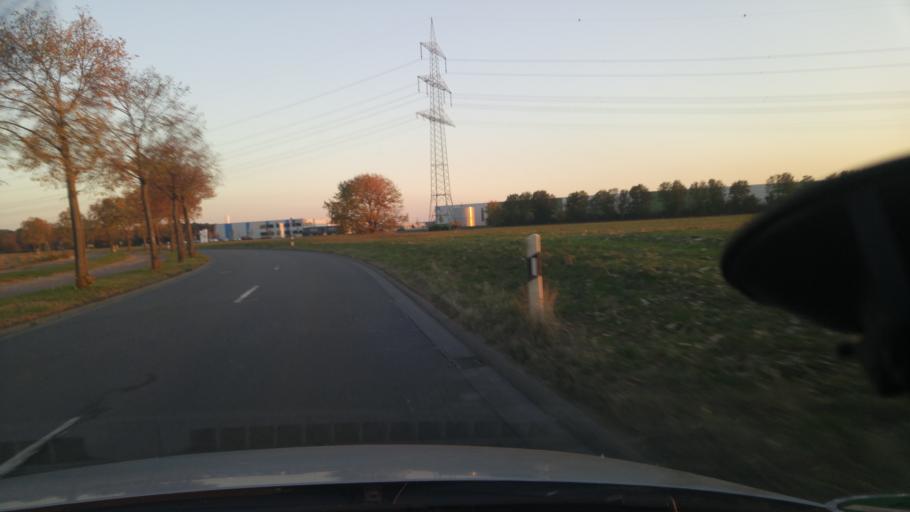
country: DE
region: Hesse
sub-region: Regierungsbezirk Darmstadt
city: Rodgau
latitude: 50.0183
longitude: 8.8999
